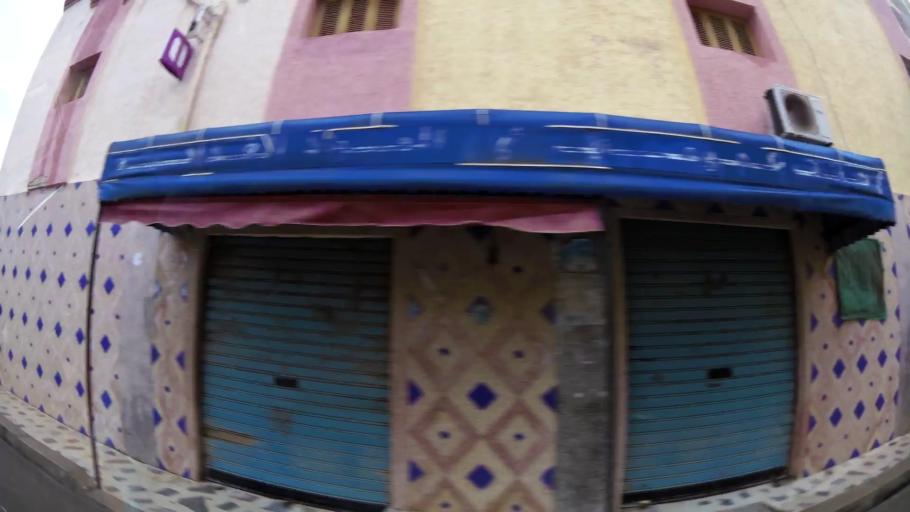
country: MA
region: Oriental
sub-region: Nador
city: Nador
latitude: 35.1468
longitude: -3.0032
